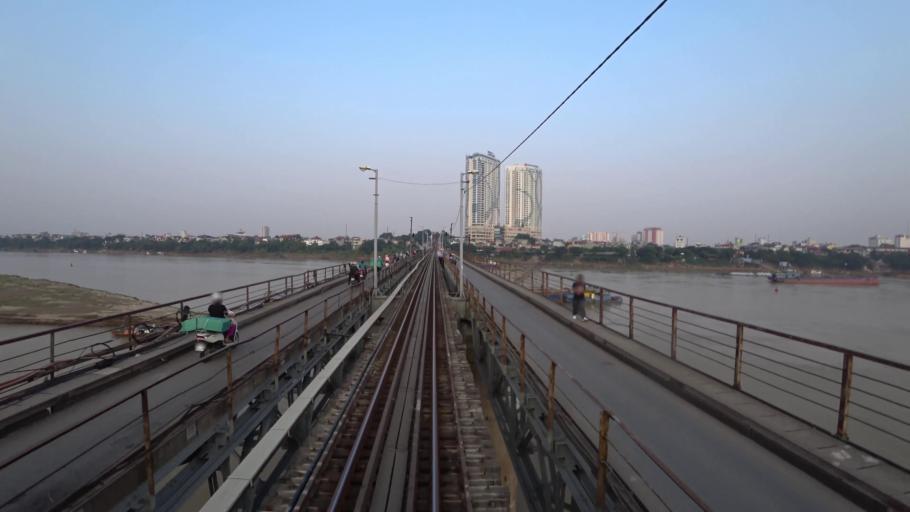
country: VN
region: Ha Noi
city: Hoan Kiem
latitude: 21.0457
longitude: 105.8645
